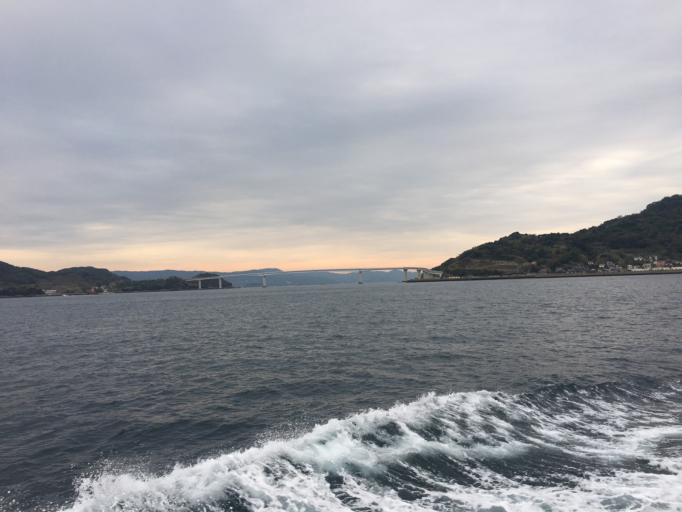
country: JP
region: Nagasaki
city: Nagasaki-shi
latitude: 32.7041
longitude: 129.7865
